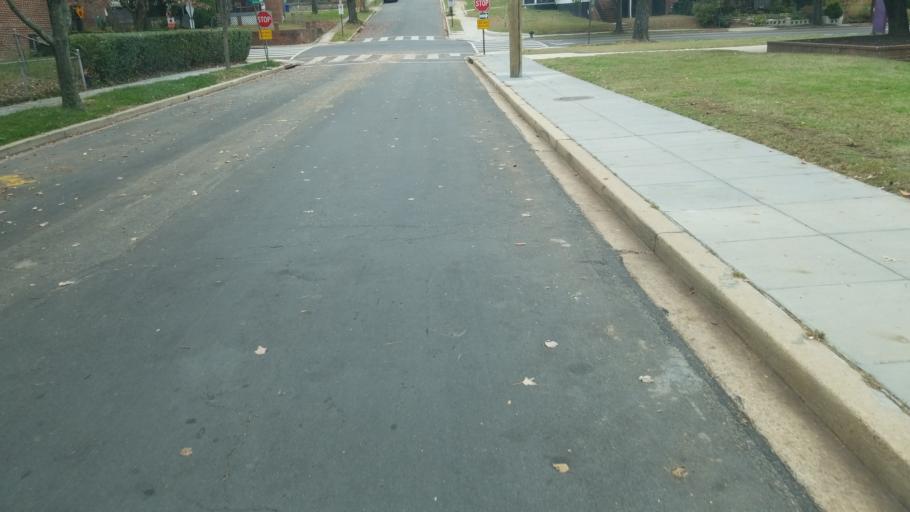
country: US
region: Maryland
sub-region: Prince George's County
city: Capitol Heights
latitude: 38.8926
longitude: -76.9323
